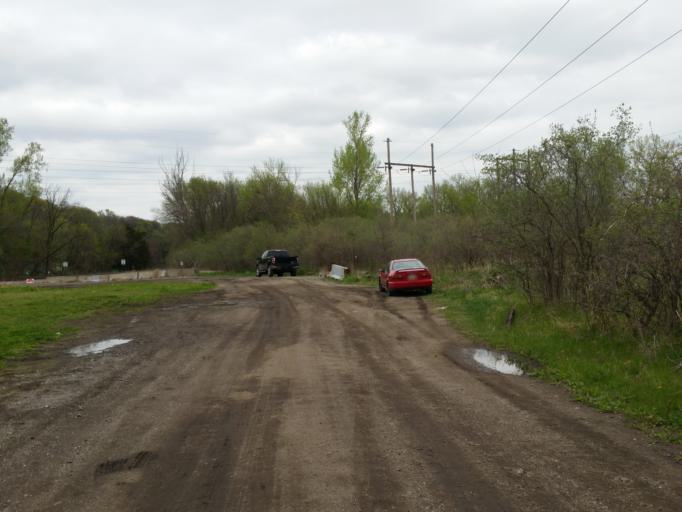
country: US
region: Nebraska
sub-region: Sarpy County
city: Bellevue
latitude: 41.1460
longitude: -95.8859
